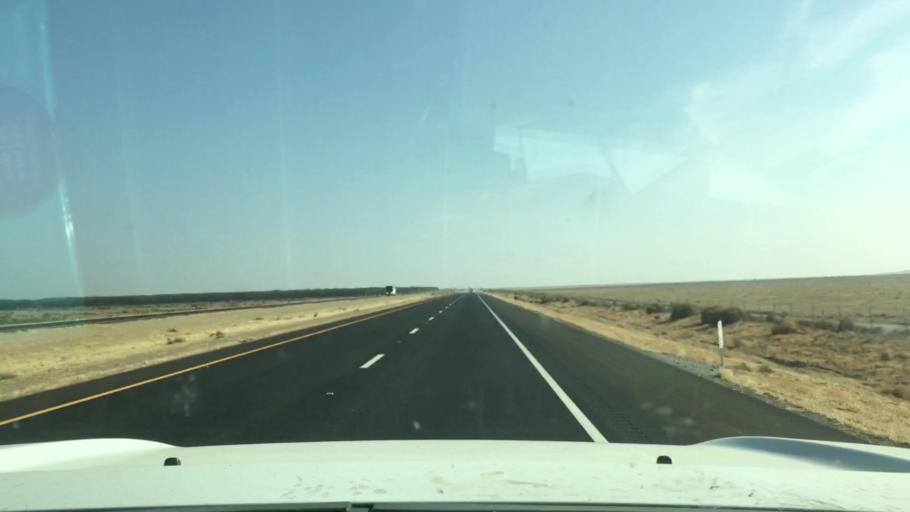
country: US
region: California
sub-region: Kern County
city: Lost Hills
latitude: 35.6220
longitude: -119.9808
